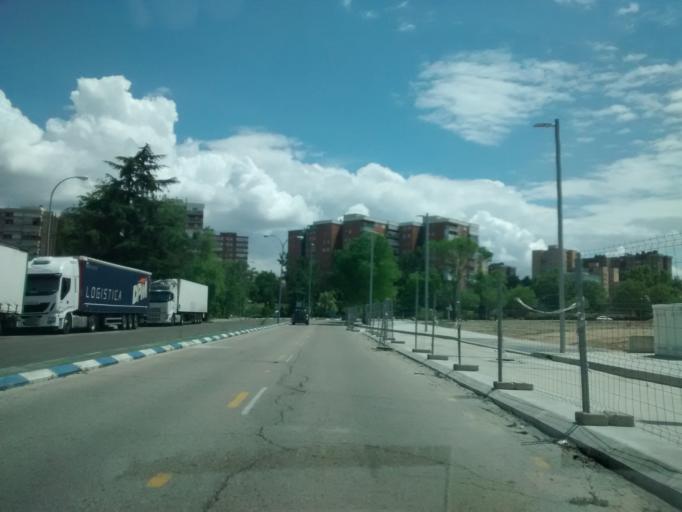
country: ES
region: Madrid
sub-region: Provincia de Madrid
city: Coslada
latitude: 40.4291
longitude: -3.5512
